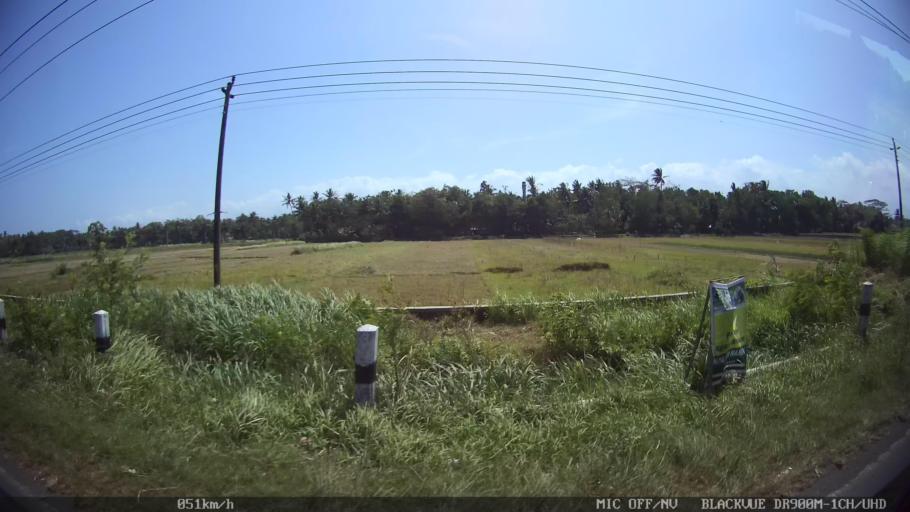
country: ID
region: Daerah Istimewa Yogyakarta
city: Srandakan
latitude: -7.9516
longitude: 110.2076
